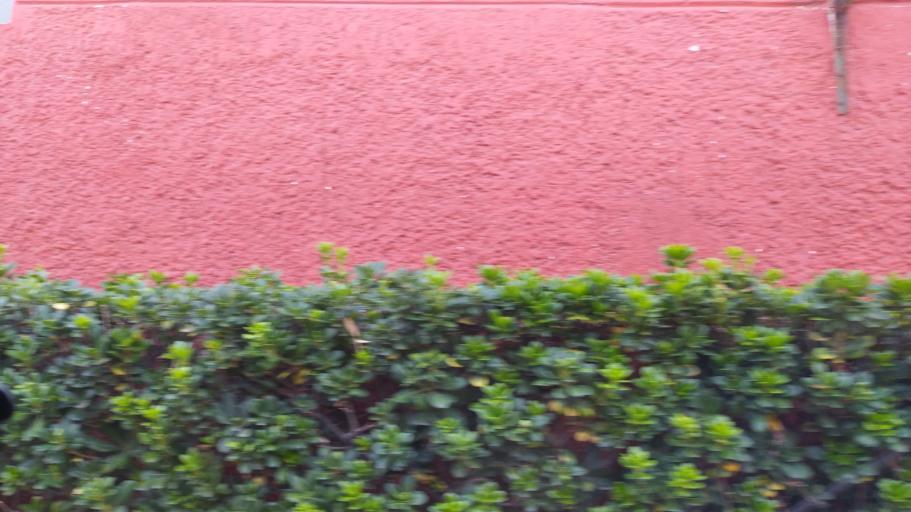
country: MX
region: Jalisco
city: Zapopan2
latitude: 20.6928
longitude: -103.4436
